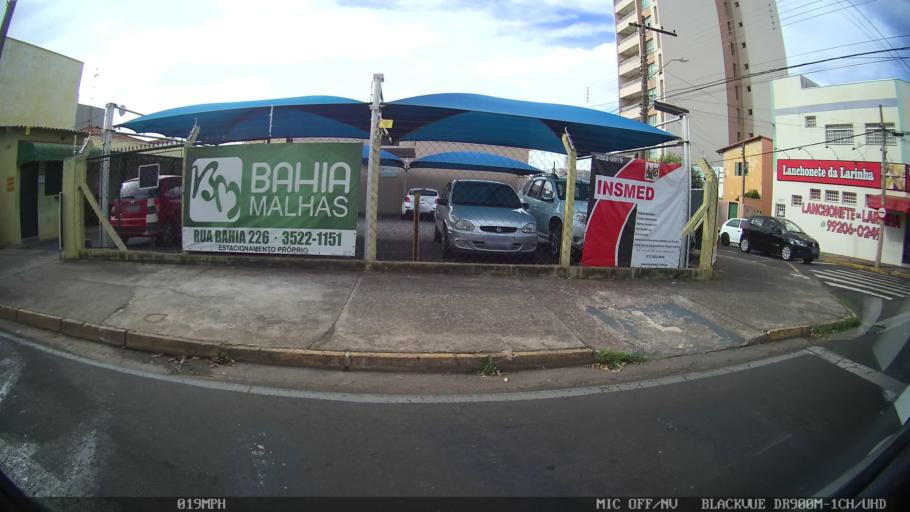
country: BR
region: Sao Paulo
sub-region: Catanduva
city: Catanduva
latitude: -21.1417
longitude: -48.9756
